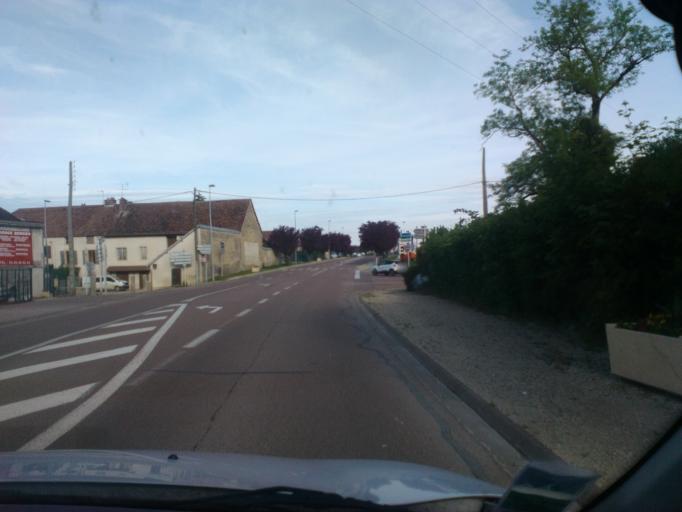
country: FR
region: Champagne-Ardenne
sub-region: Departement de l'Aube
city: Vendeuvre-sur-Barse
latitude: 48.2397
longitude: 4.4750
